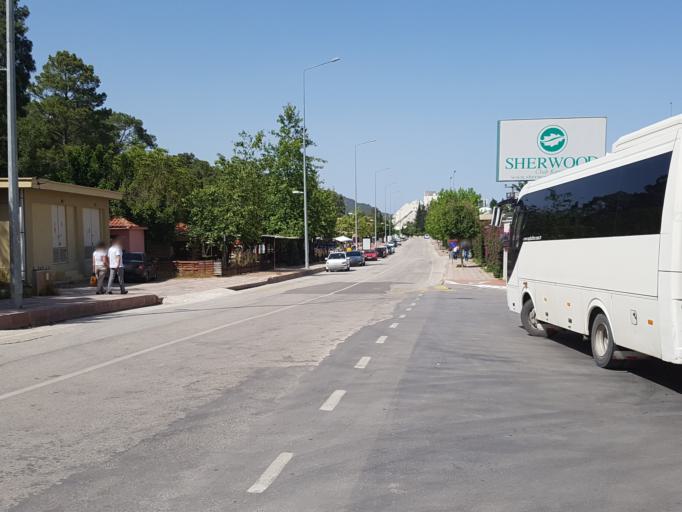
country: TR
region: Antalya
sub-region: Kemer
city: Goeynuek
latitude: 36.6542
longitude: 30.5540
